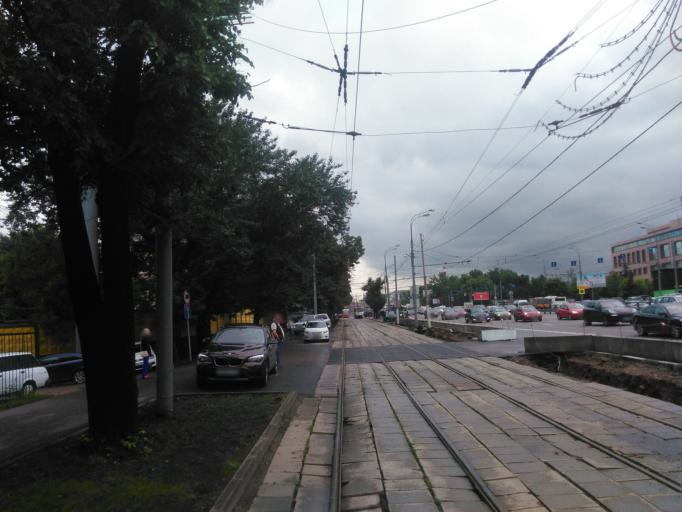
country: RU
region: Moscow
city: Kotlovka
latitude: 55.6856
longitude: 37.6233
